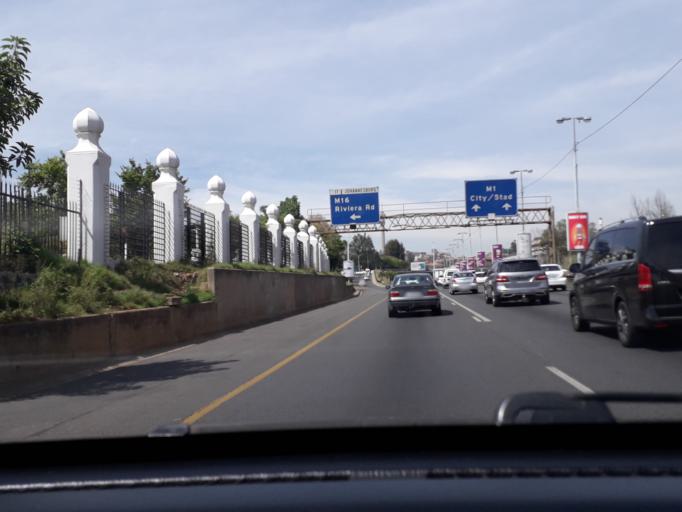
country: ZA
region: Gauteng
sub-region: City of Johannesburg Metropolitan Municipality
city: Johannesburg
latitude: -26.1625
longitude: 28.0570
